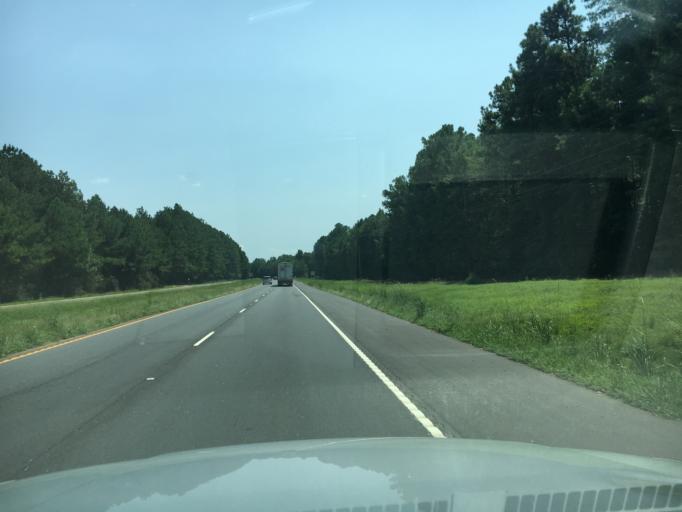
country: US
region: South Carolina
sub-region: Anderson County
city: Pendleton
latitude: 34.6538
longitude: -82.8104
